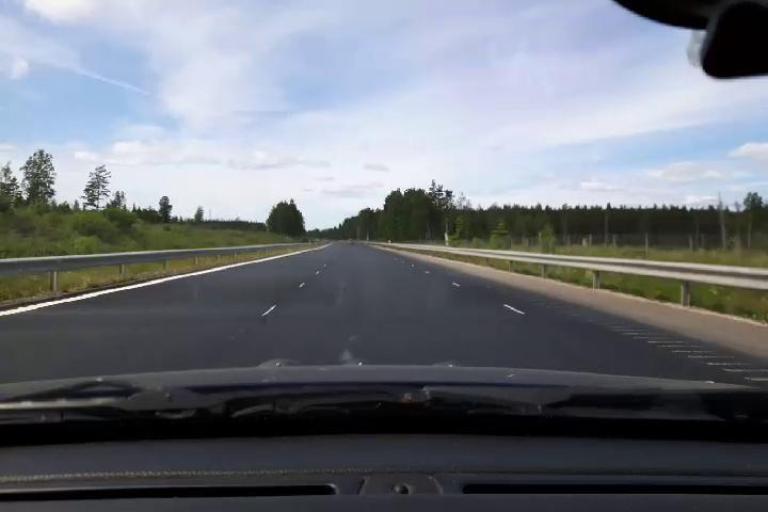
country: SE
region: Gaevleborg
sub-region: Gavle Kommun
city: Gavle
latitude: 60.5759
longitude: 17.2252
